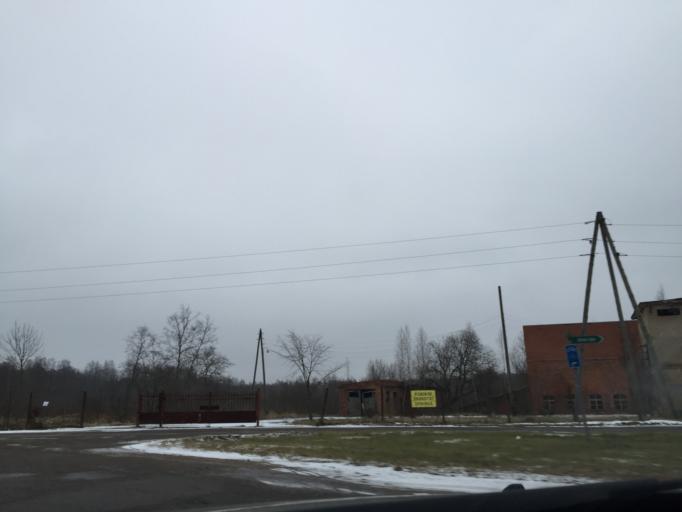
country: LV
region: Saulkrastu
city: Saulkrasti
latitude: 57.4889
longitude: 24.3909
